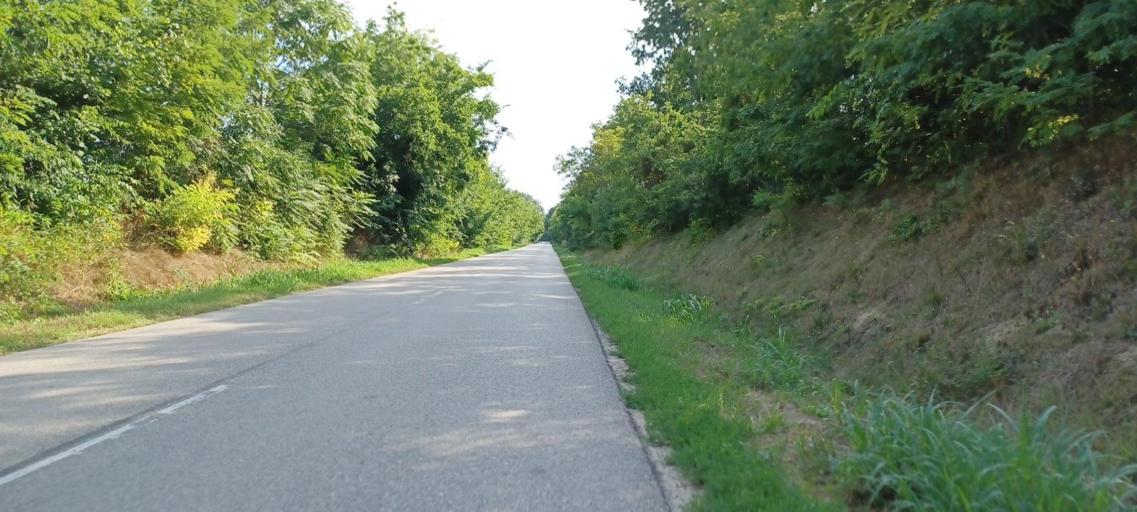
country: HU
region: Tolna
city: Tengelic
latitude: 46.5498
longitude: 18.7129
